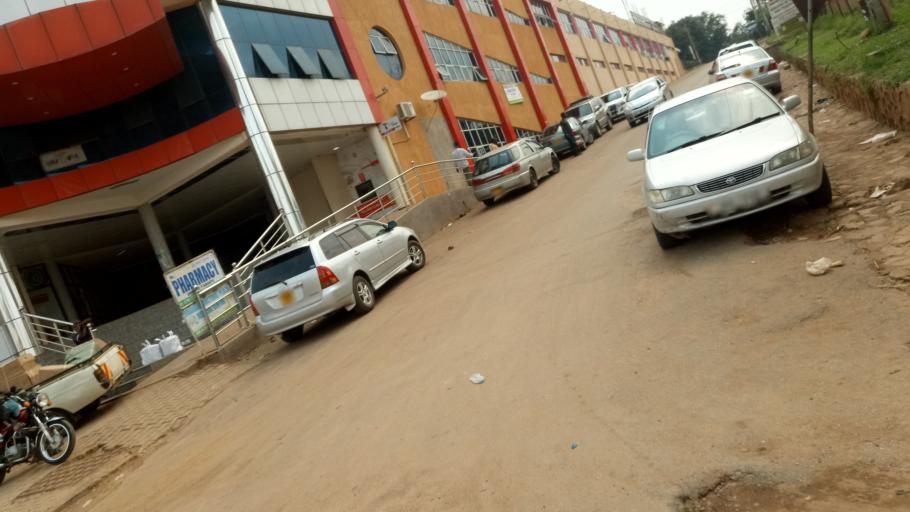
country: UG
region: Western Region
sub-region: Mbarara District
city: Mbarara
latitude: -0.6129
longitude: 30.6601
